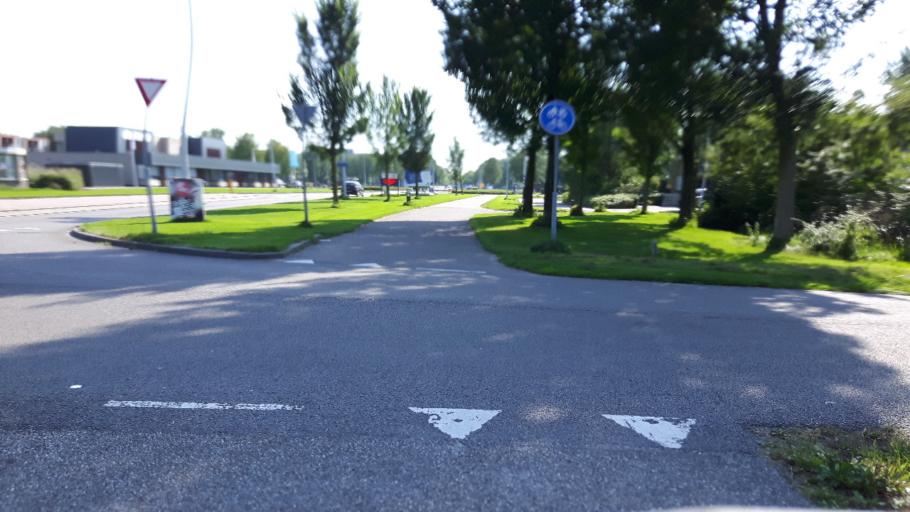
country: NL
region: Friesland
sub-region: Gemeente Franekeradeel
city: Franeker
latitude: 53.1974
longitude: 5.5409
